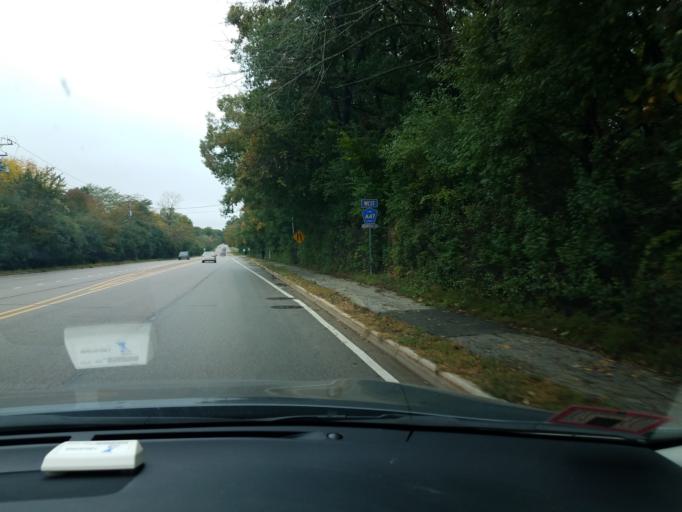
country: US
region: Illinois
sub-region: Lake County
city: Riverwoods
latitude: 42.1676
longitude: -87.8835
